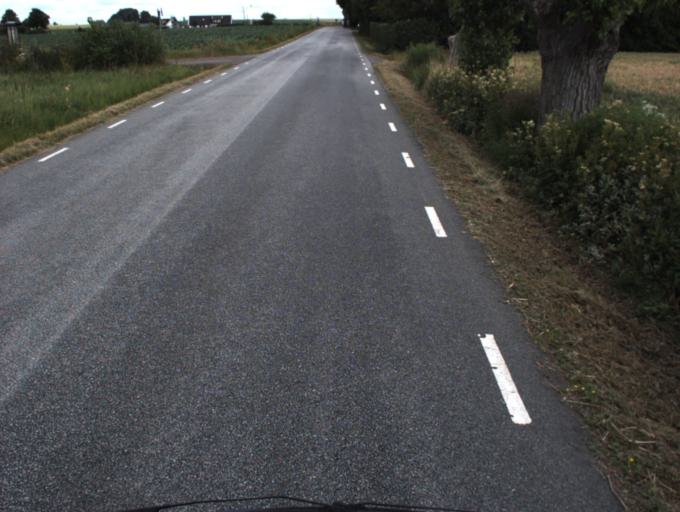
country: SE
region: Skane
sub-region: Helsingborg
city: Rydeback
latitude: 55.9582
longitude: 12.7808
